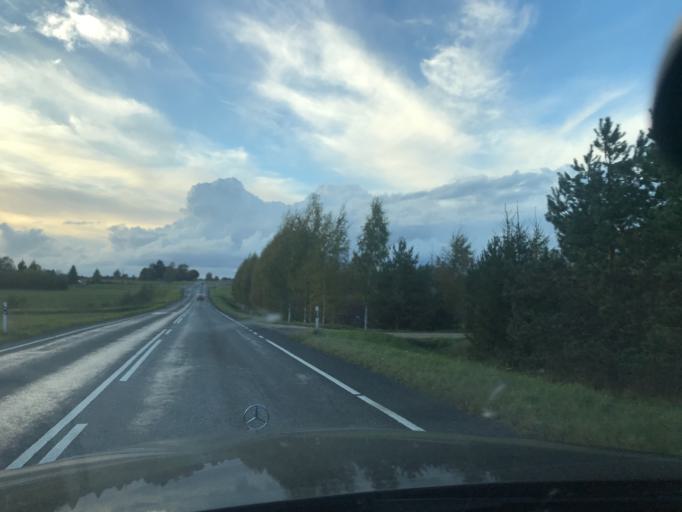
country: EE
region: Vorumaa
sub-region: Antsla vald
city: Vana-Antsla
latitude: 57.8834
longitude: 26.5321
